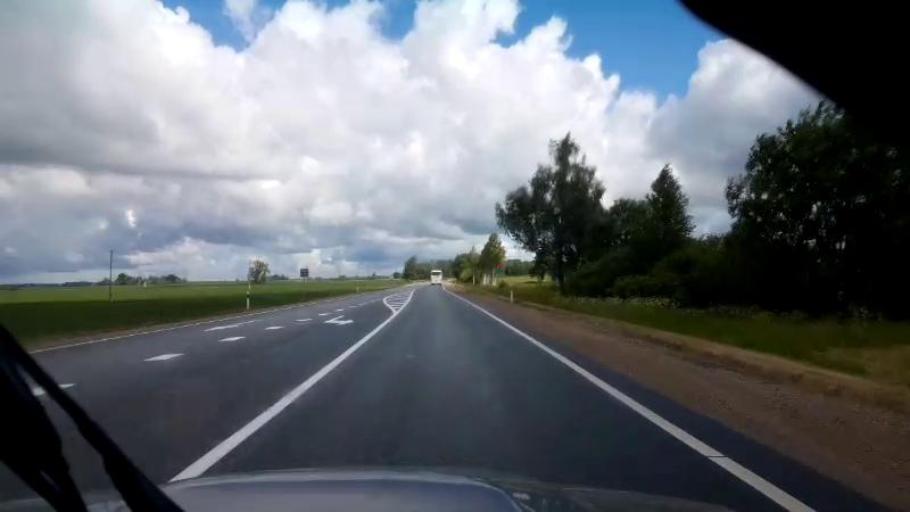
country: LV
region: Lecava
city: Iecava
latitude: 56.5073
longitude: 24.1731
